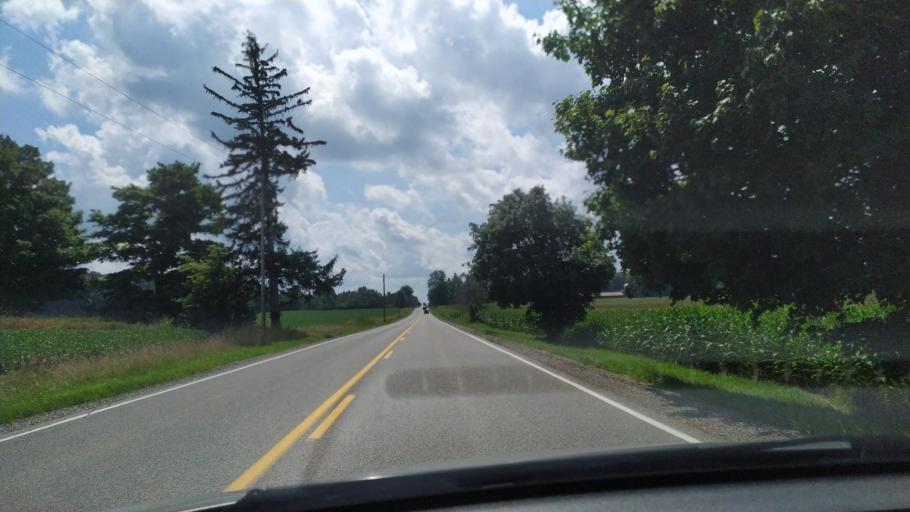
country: CA
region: Ontario
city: London
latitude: 43.0531
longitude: -81.3287
